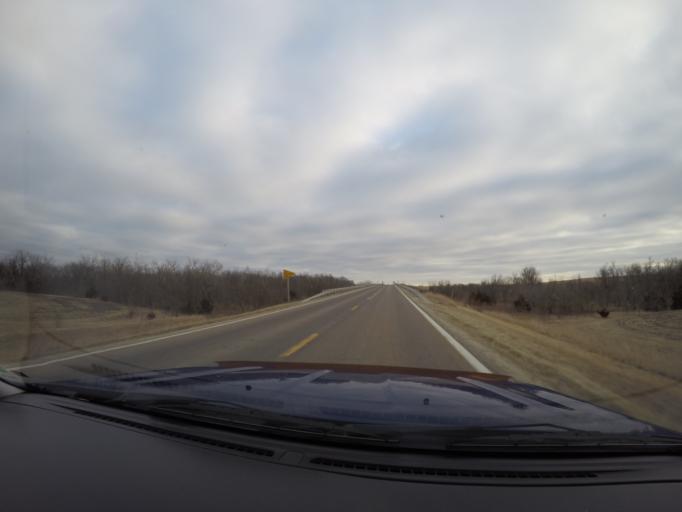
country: US
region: Kansas
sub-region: Morris County
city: Council Grove
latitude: 38.8595
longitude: -96.5040
